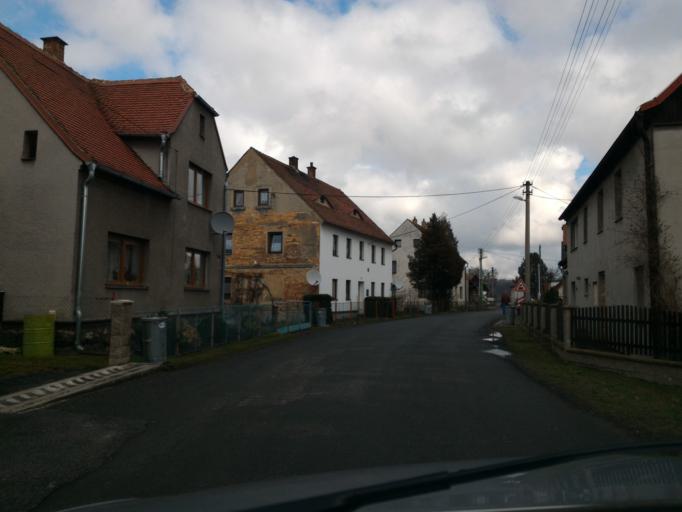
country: CZ
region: Liberecky
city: Visnova
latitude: 50.9675
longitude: 15.0268
